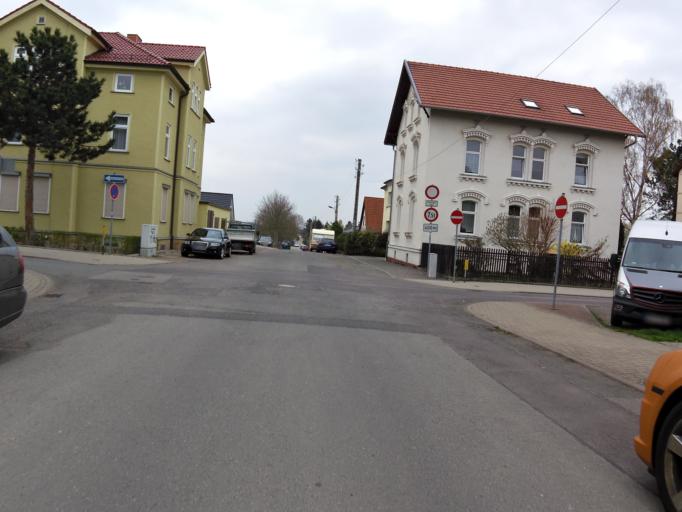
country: DE
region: Thuringia
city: Gotha
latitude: 50.9542
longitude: 10.7021
